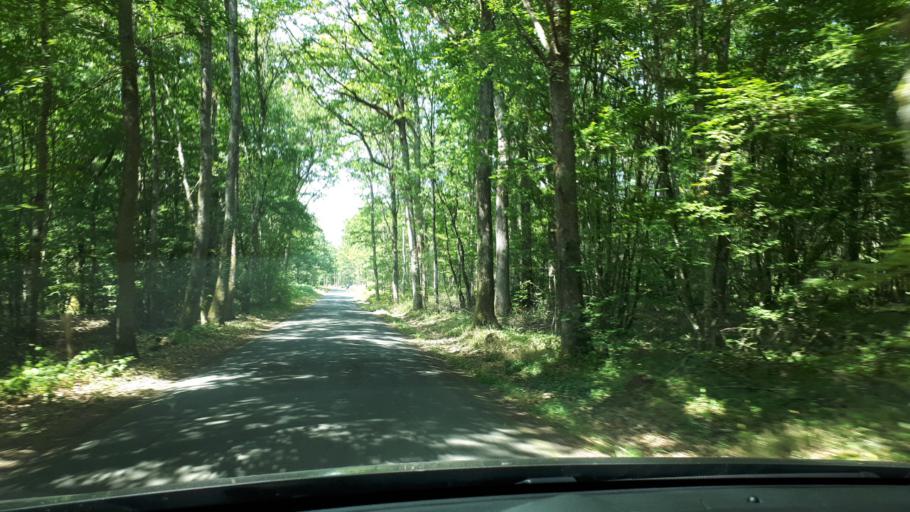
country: FR
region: Centre
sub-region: Departement du Loir-et-Cher
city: Naveil
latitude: 47.8267
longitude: 1.0408
